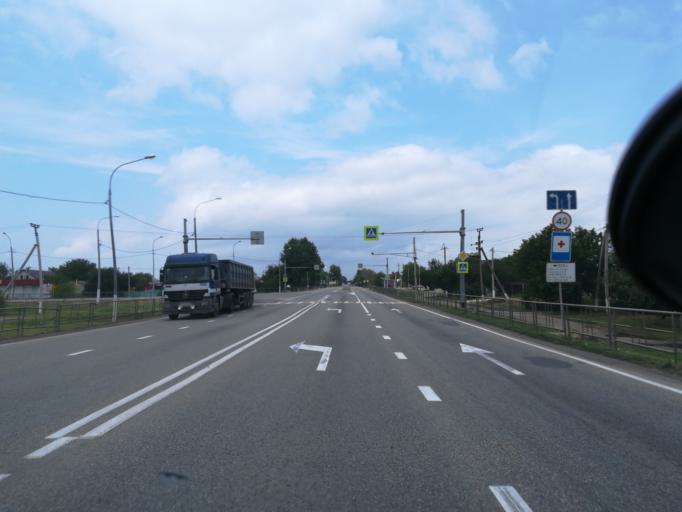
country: RU
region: Krasnodarskiy
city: Korzhevskiy
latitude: 45.1981
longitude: 37.6634
